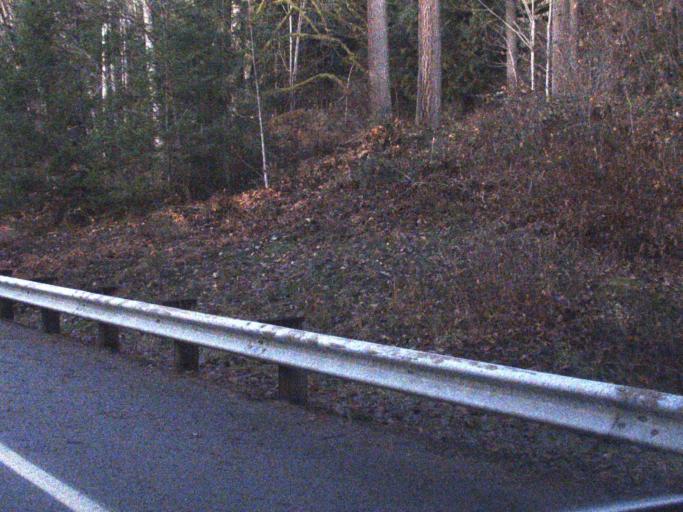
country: US
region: Washington
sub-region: Snohomish County
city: Darrington
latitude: 48.5071
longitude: -121.6557
